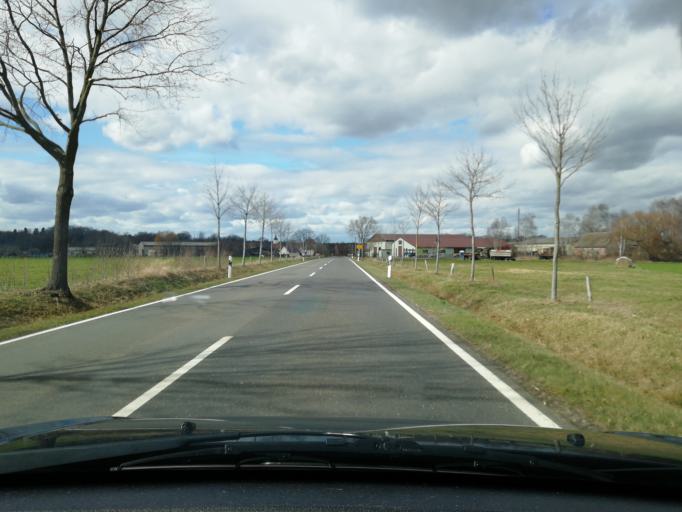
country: DE
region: Brandenburg
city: Altdobern
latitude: 51.7096
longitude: 14.0521
